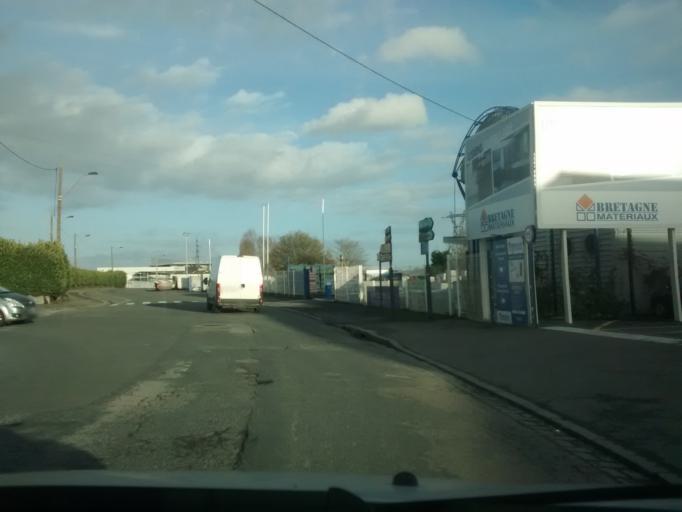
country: FR
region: Brittany
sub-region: Departement d'Ille-et-Vilaine
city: Vezin-le-Coquet
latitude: 48.1027
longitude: -1.7235
